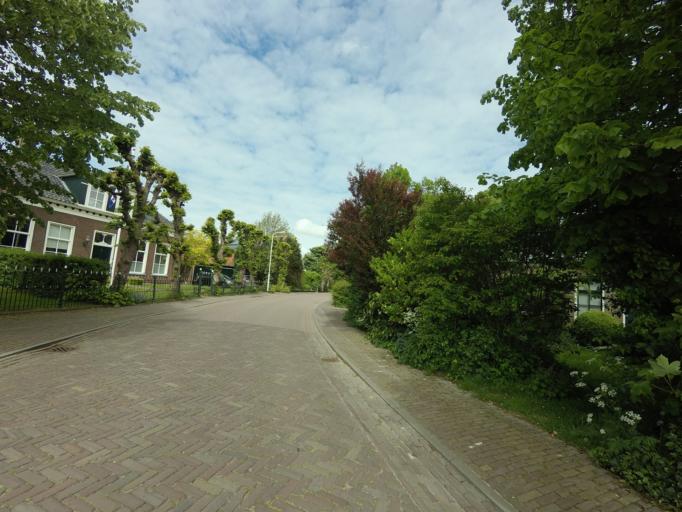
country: NL
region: Friesland
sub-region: Gemeente Gaasterlan-Sleat
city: Balk
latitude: 52.9211
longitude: 5.5376
